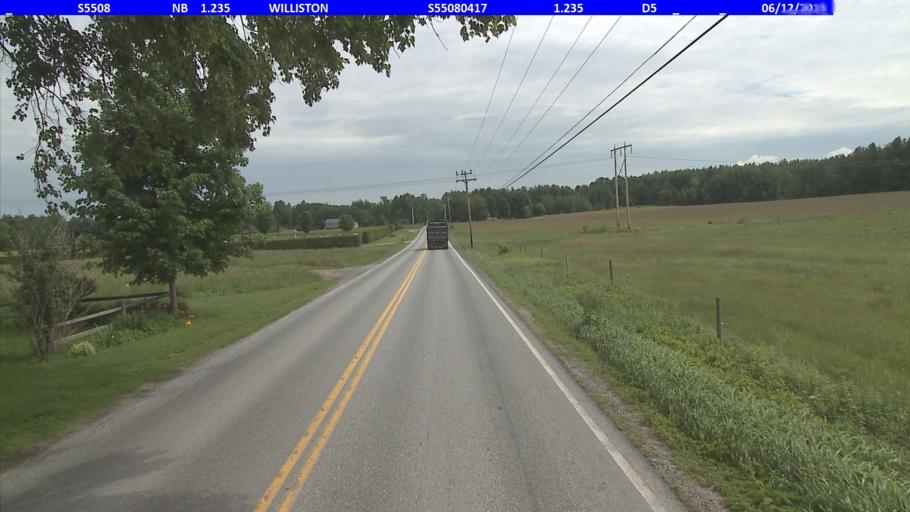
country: US
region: Vermont
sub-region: Chittenden County
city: Williston
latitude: 44.4533
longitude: -73.0573
